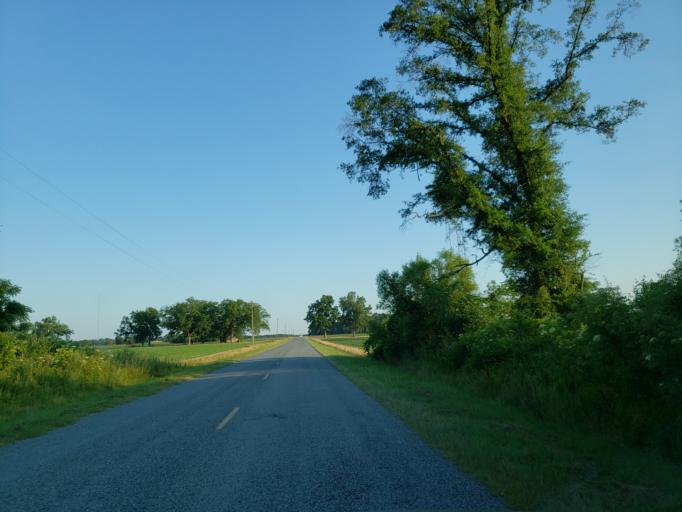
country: US
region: Georgia
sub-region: Dooly County
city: Vienna
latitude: 32.0976
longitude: -83.7564
